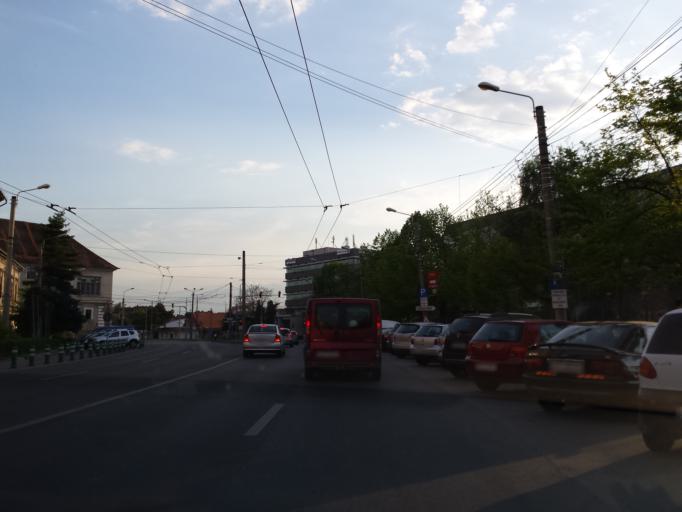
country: RO
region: Timis
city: Timisoara
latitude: 45.7586
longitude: 21.2260
